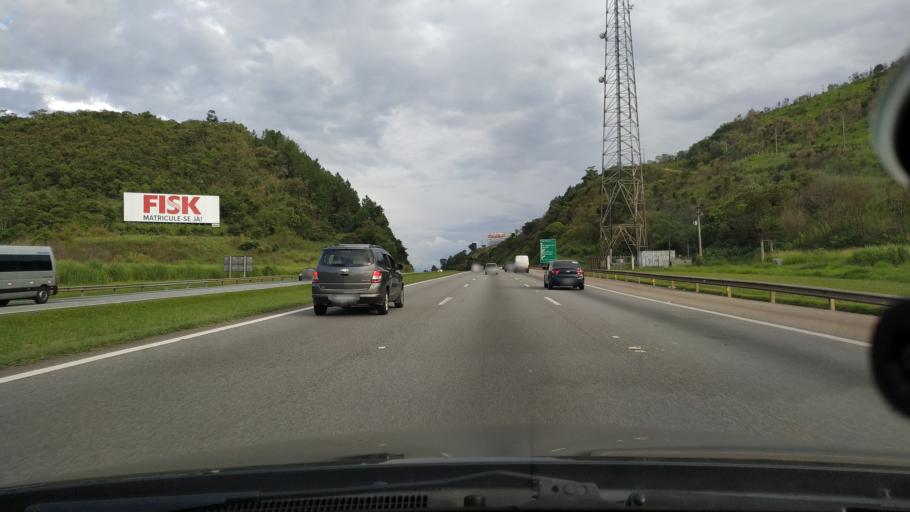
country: BR
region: Sao Paulo
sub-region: Sao Roque
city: Sao Roque
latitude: -23.4353
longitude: -47.1212
